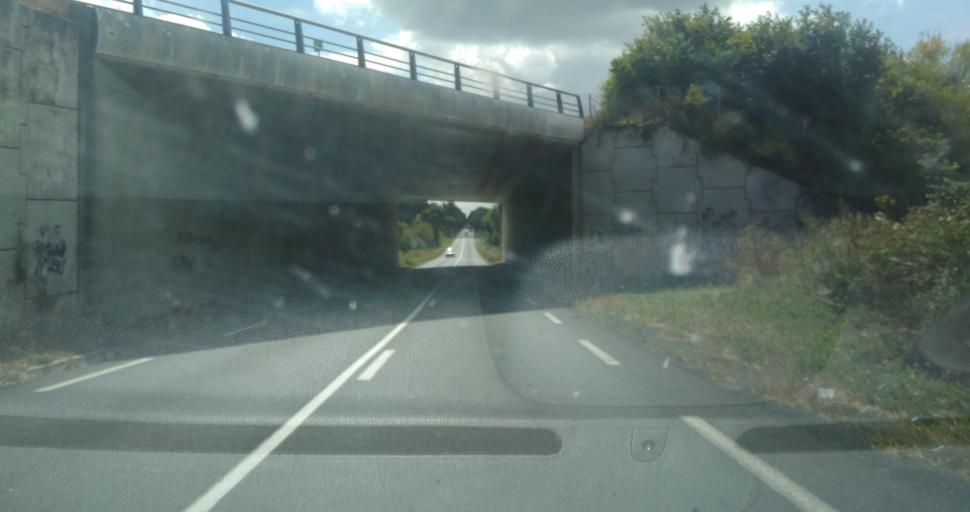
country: FR
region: Pays de la Loire
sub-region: Departement de la Vendee
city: Bournezeau
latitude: 46.6059
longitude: -1.1392
